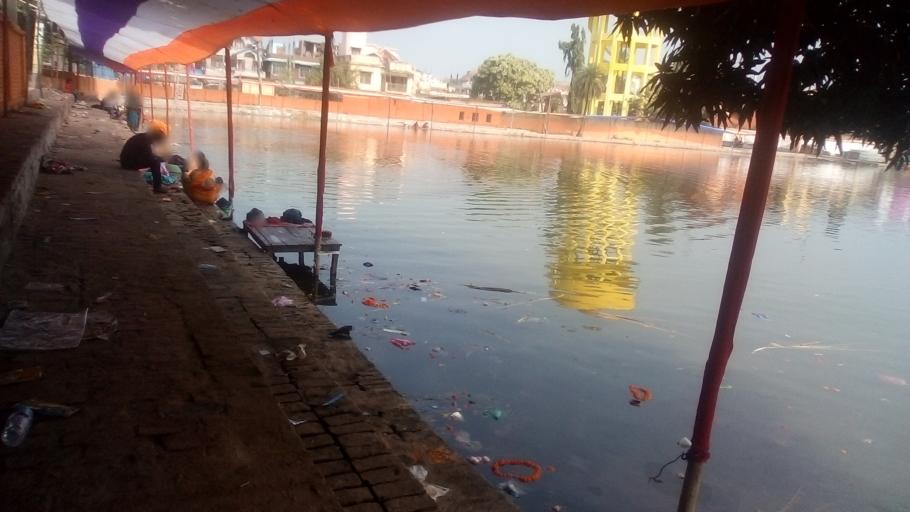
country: NP
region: Central Region
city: Janakpur
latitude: 26.7320
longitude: 85.9247
